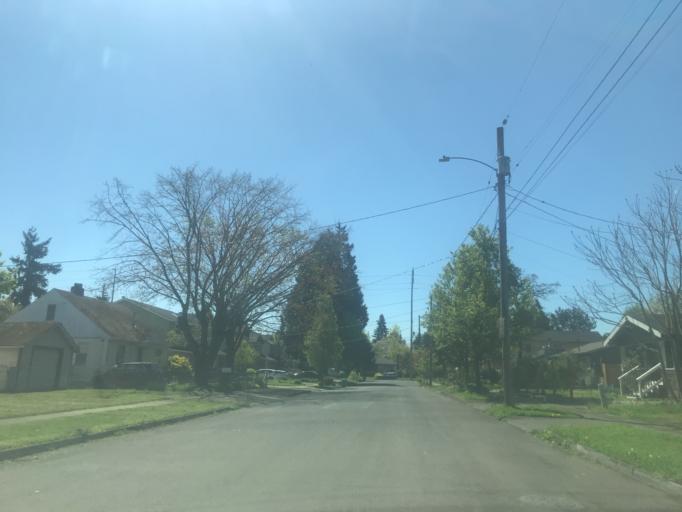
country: US
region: Oregon
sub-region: Multnomah County
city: Lents
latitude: 45.4830
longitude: -122.5932
